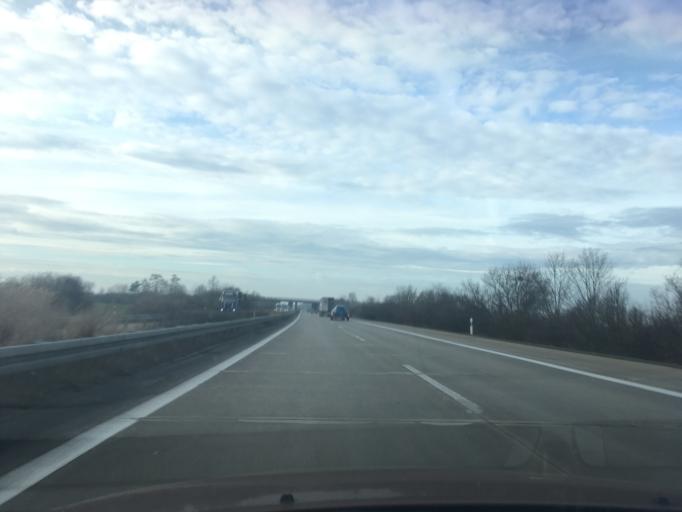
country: DE
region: Saxony
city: Guttau
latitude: 51.2118
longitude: 14.5655
